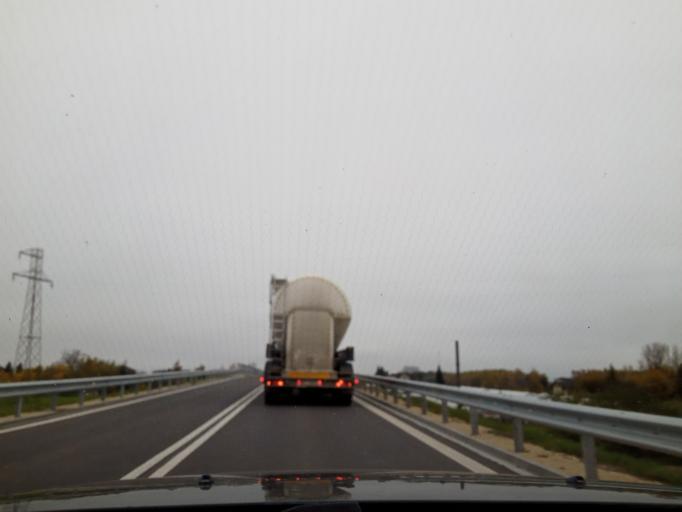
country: PL
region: Swietokrzyskie
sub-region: Powiat jedrzejowski
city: Jedrzejow
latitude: 50.6084
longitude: 20.3161
